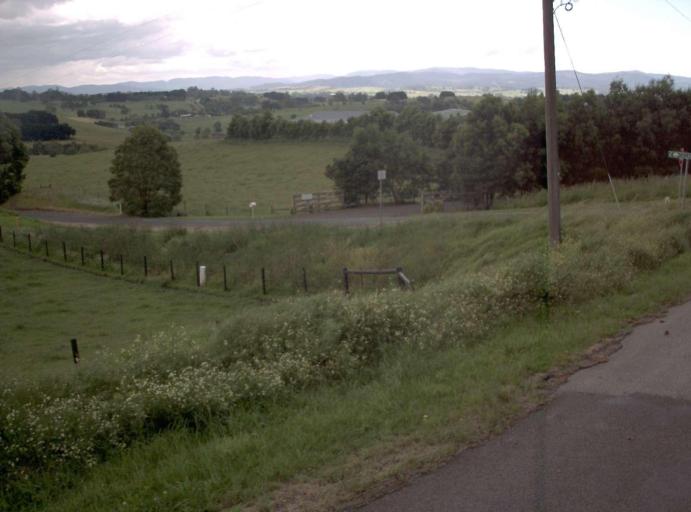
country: AU
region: Victoria
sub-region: Baw Baw
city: Warragul
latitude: -38.1117
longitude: 145.9256
